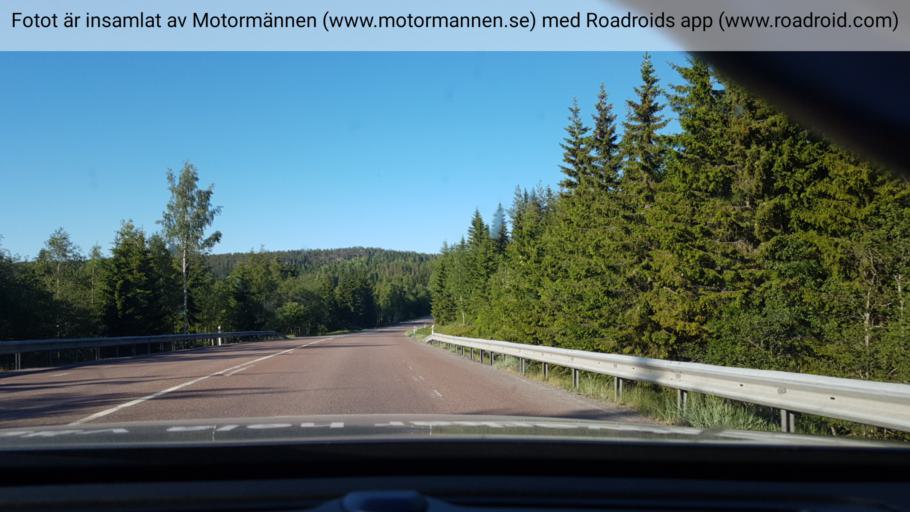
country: SE
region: Vaesternorrland
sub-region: Haernoesands Kommun
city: Haernoesand
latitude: 62.7012
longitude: 17.8569
